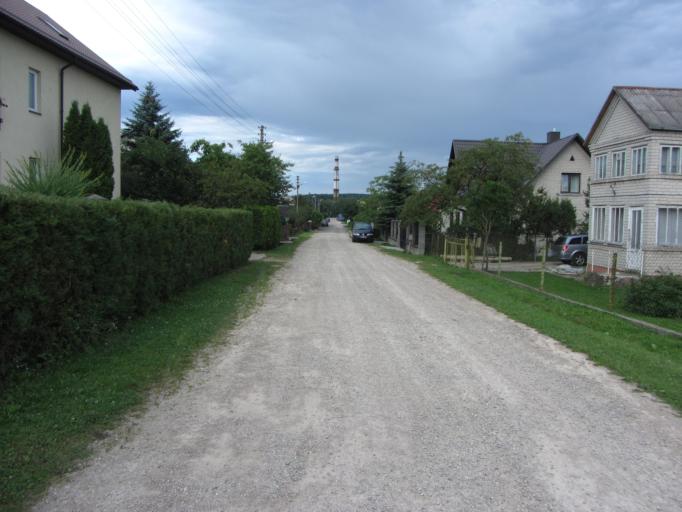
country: LT
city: Grigiskes
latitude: 54.6703
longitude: 25.0806
